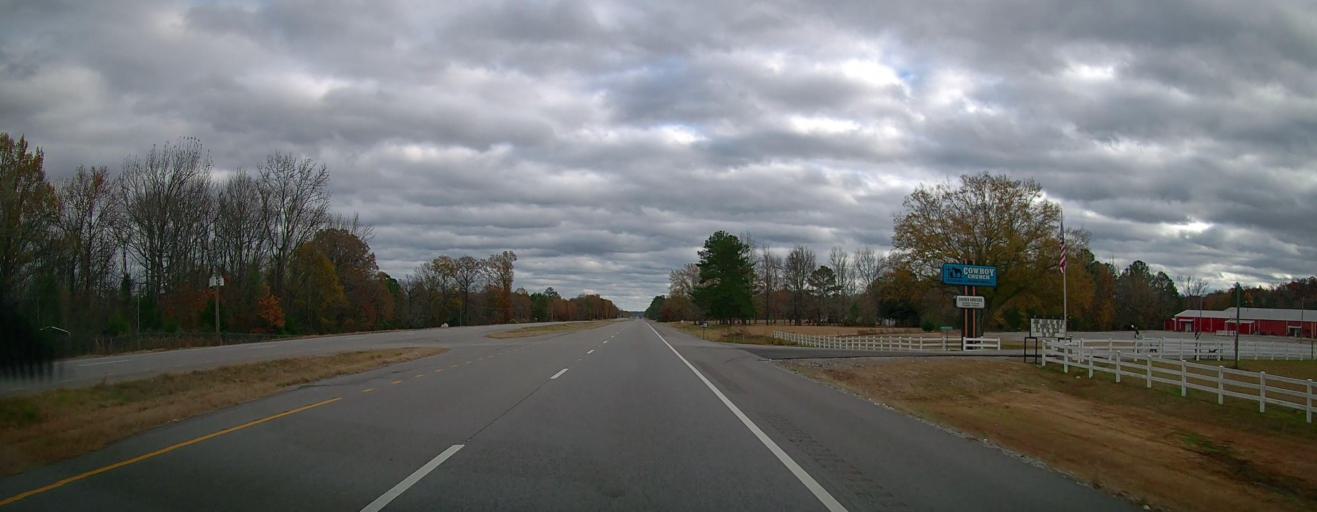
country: US
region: Alabama
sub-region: Lawrence County
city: Town Creek
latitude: 34.6617
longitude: -87.5449
